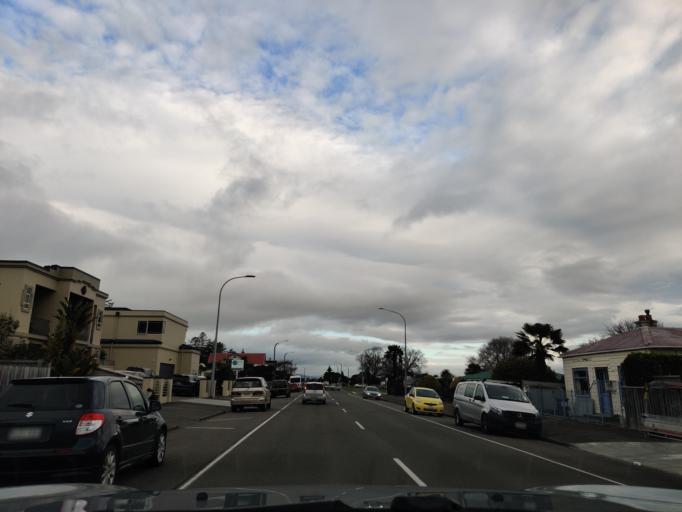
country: NZ
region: Hawke's Bay
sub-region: Napier City
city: Napier
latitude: -39.4989
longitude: 176.9177
